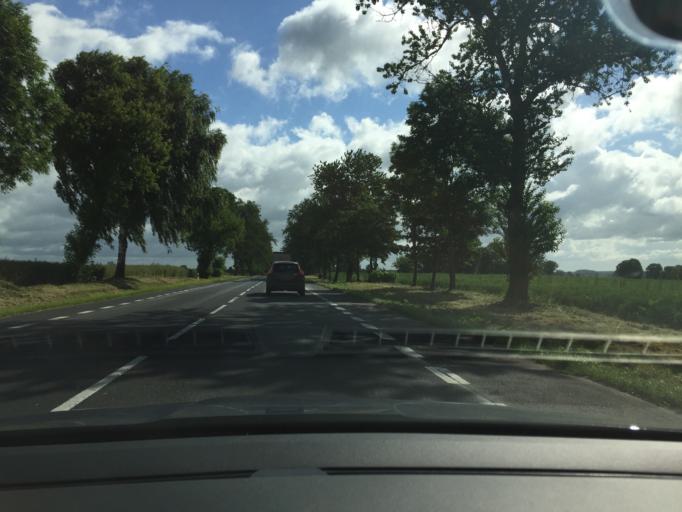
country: PL
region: West Pomeranian Voivodeship
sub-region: Powiat kolobrzeski
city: Goscino
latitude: 53.9774
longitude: 15.6855
